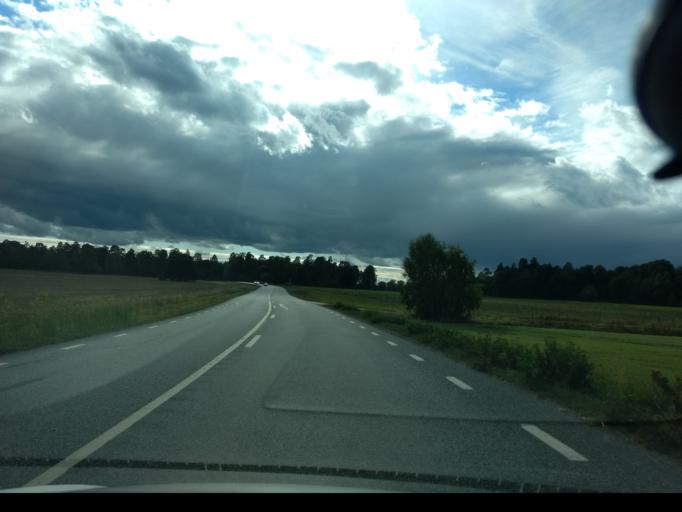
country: SE
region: Uppsala
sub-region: Uppsala Kommun
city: Saevja
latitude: 59.7687
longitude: 17.6496
